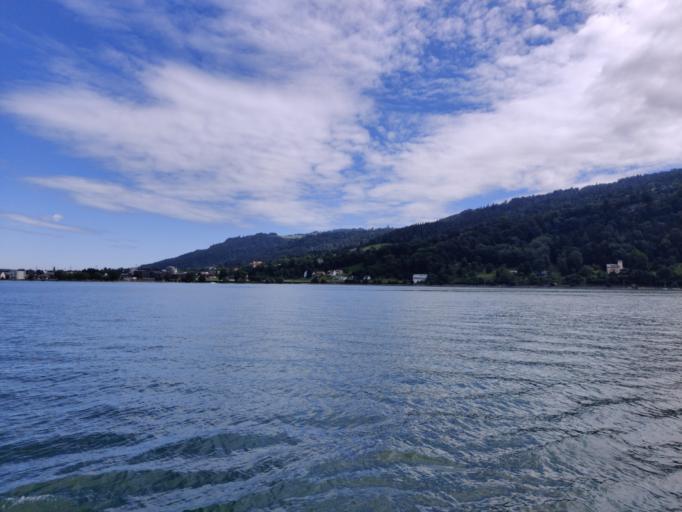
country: AT
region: Vorarlberg
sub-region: Politischer Bezirk Bregenz
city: Bregenz
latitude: 47.5153
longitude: 9.7426
